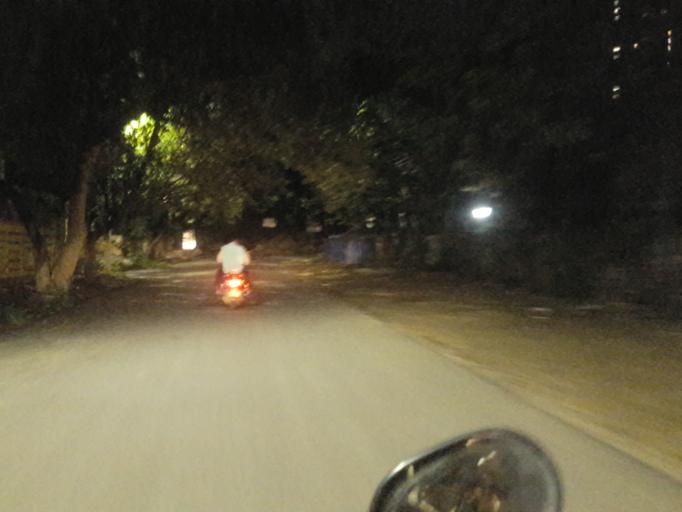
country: IN
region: Telangana
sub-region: Rangareddi
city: Kukatpalli
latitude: 17.4777
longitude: 78.3937
